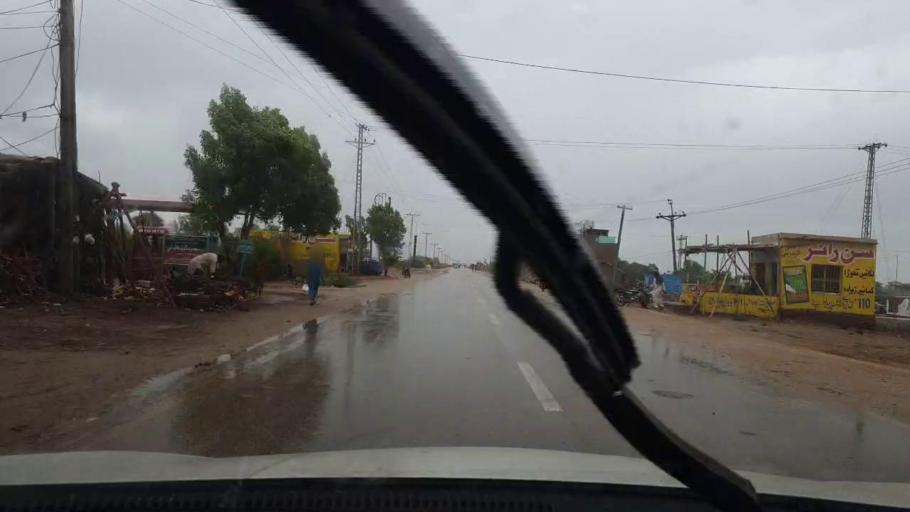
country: PK
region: Sindh
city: Kario
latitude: 24.6535
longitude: 68.5417
